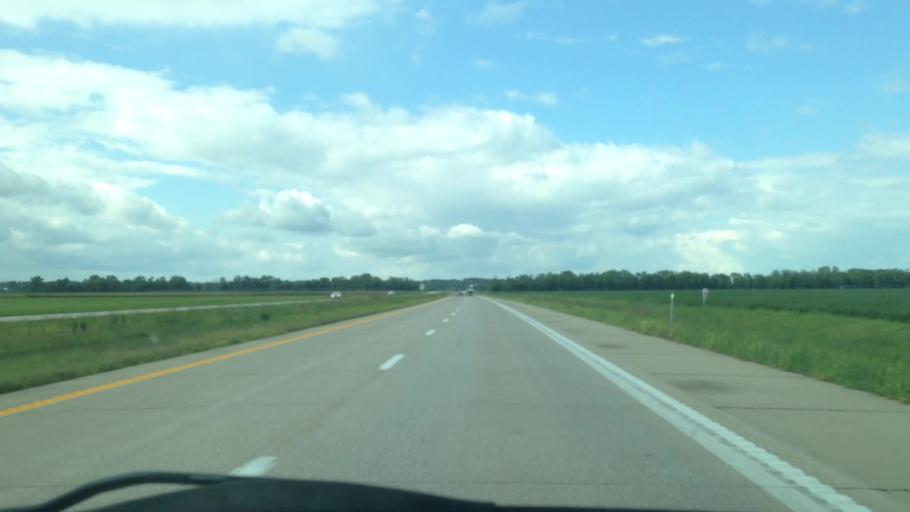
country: US
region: Illinois
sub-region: Hancock County
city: Warsaw
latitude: 40.4068
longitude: -91.5721
